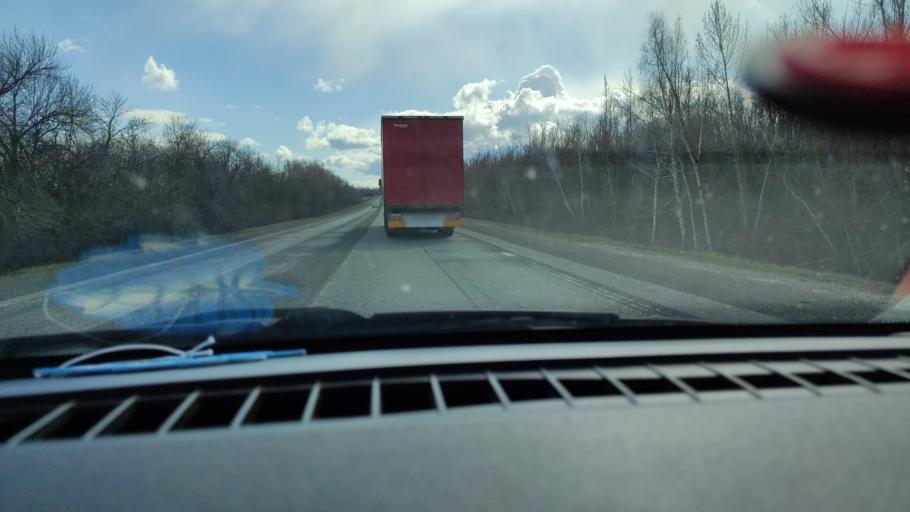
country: RU
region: Saratov
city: Dukhovnitskoye
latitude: 52.6263
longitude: 48.1801
